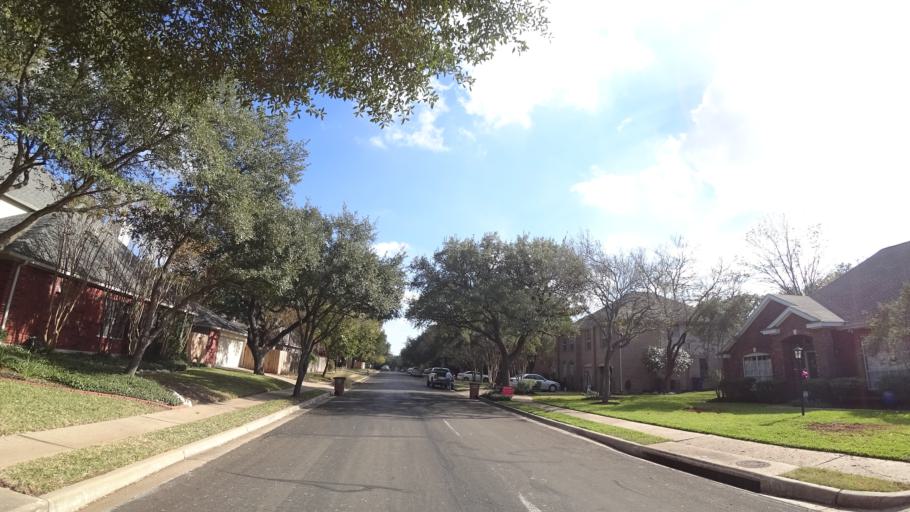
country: US
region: Texas
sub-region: Travis County
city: Shady Hollow
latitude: 30.1823
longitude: -97.8608
